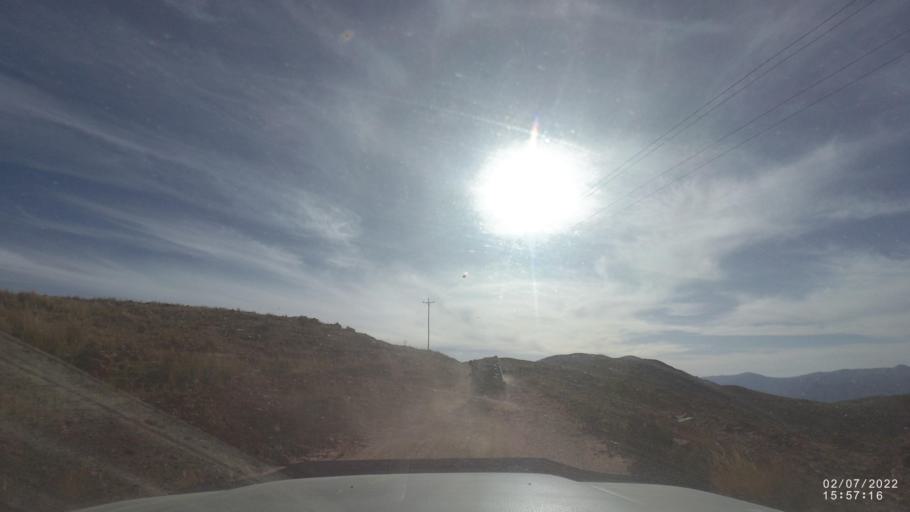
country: BO
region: Cochabamba
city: Irpa Irpa
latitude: -17.9082
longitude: -66.4281
